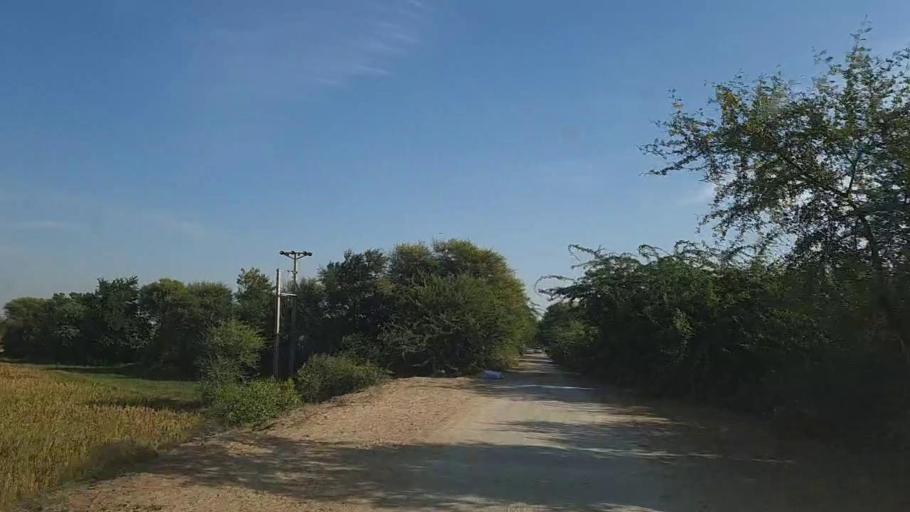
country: PK
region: Sindh
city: Bulri
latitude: 24.7943
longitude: 68.3414
